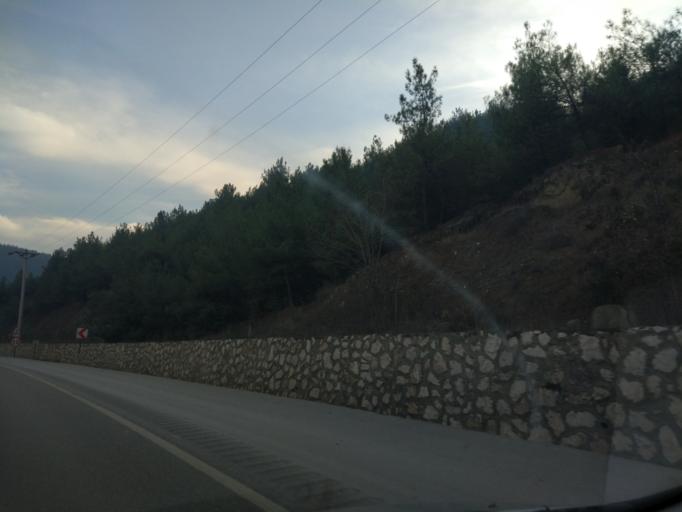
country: TR
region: Karabuk
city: Karabuk
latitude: 41.1597
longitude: 32.6408
